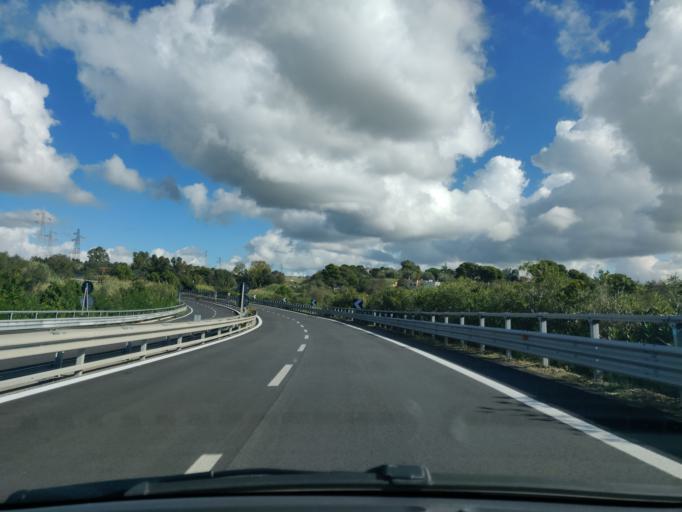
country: IT
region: Latium
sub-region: Citta metropolitana di Roma Capitale
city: Civitavecchia
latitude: 42.1065
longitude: 11.7909
